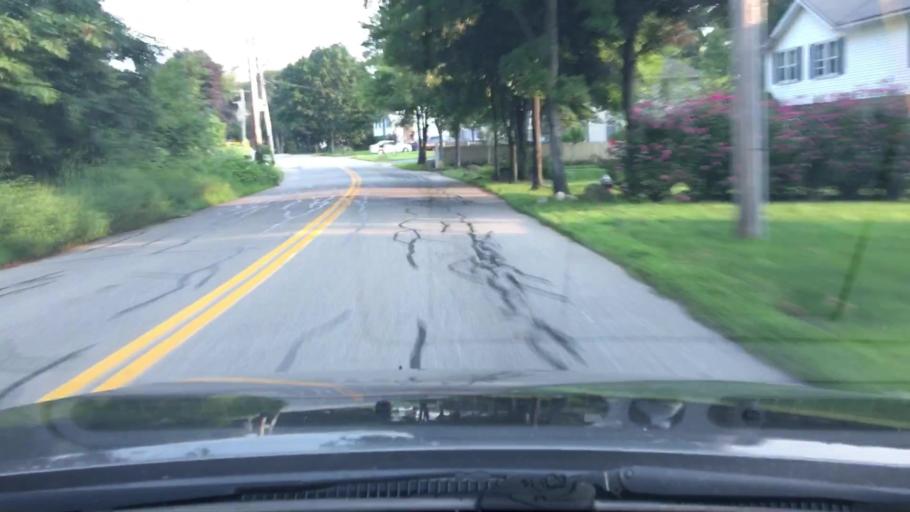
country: US
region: Massachusetts
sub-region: Worcester County
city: Hopedale
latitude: 42.1601
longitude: -71.5380
